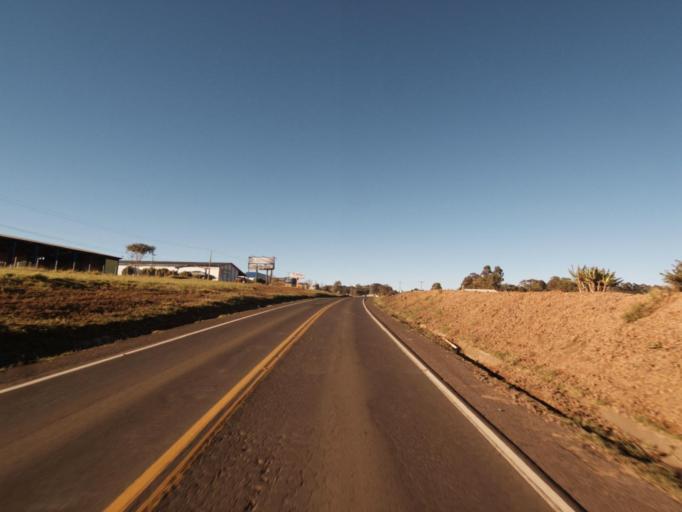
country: AR
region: Misiones
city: Bernardo de Irigoyen
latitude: -26.4302
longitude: -53.5196
